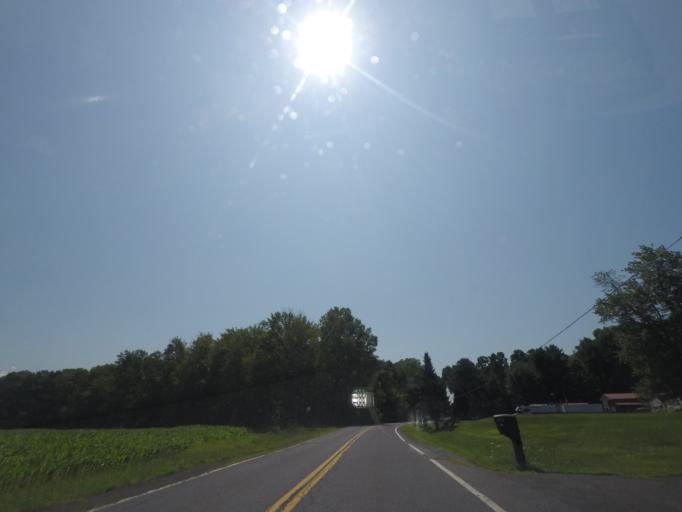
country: US
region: New York
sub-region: Saratoga County
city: Mechanicville
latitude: 42.8560
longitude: -73.7199
